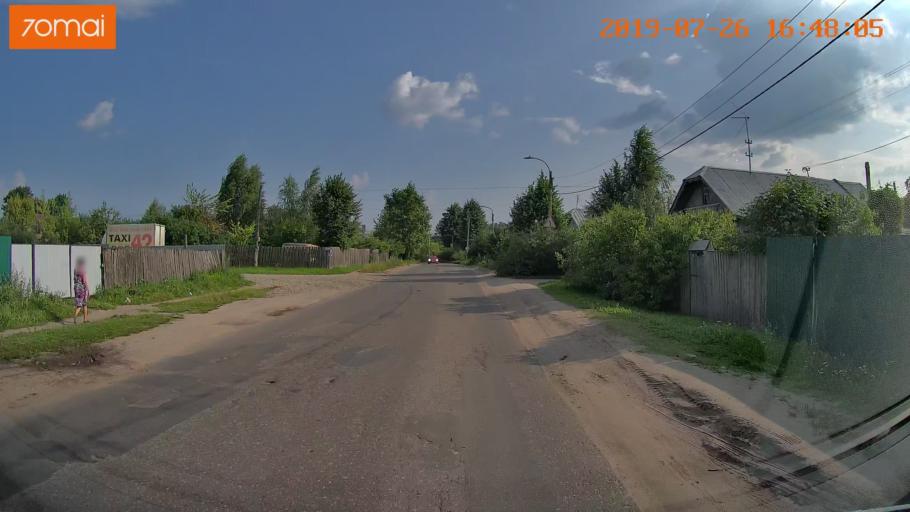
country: RU
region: Ivanovo
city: Bogorodskoye
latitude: 57.0370
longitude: 41.0125
